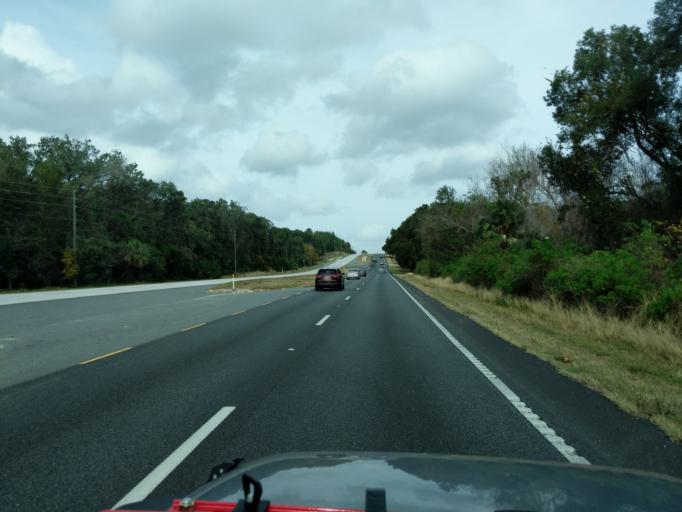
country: US
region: Florida
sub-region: Orange County
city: Tangerine
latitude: 28.7568
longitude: -81.6244
